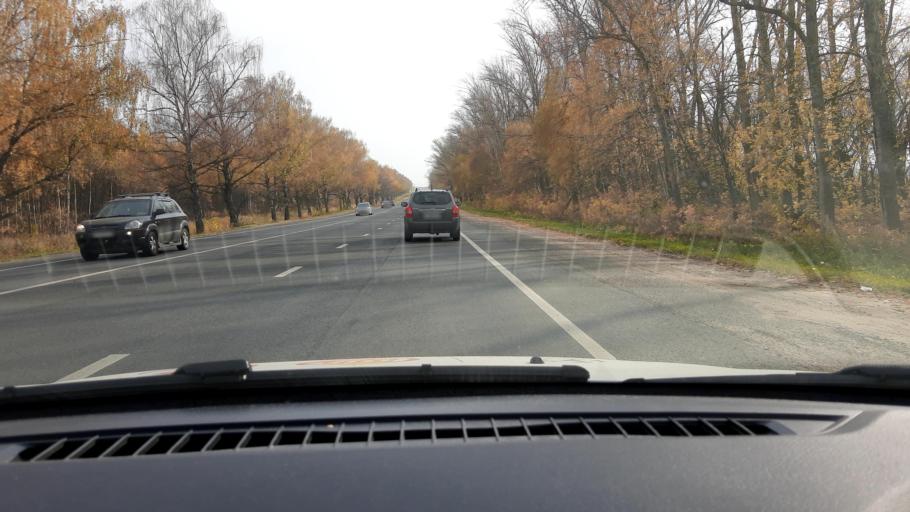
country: RU
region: Nizjnij Novgorod
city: Kstovo
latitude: 56.1400
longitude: 44.2304
